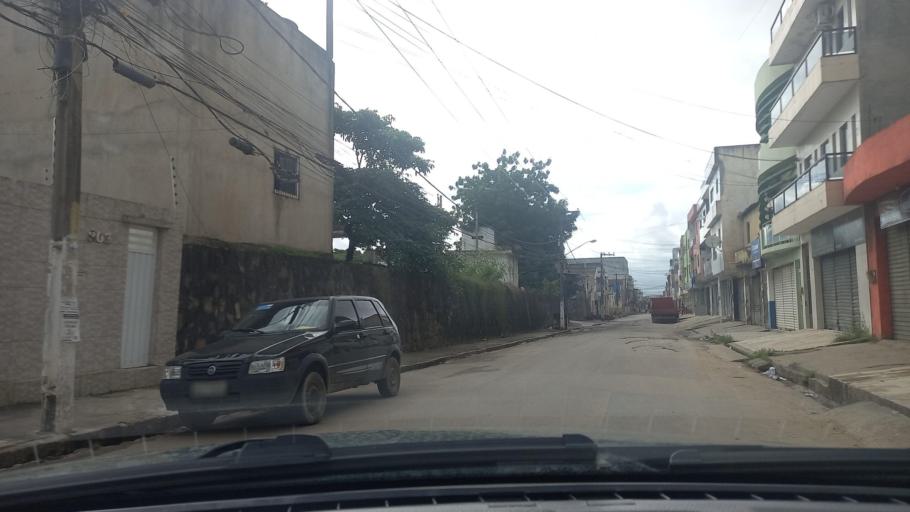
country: BR
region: Pernambuco
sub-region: Vitoria De Santo Antao
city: Vitoria de Santo Antao
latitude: -8.1185
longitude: -35.3043
